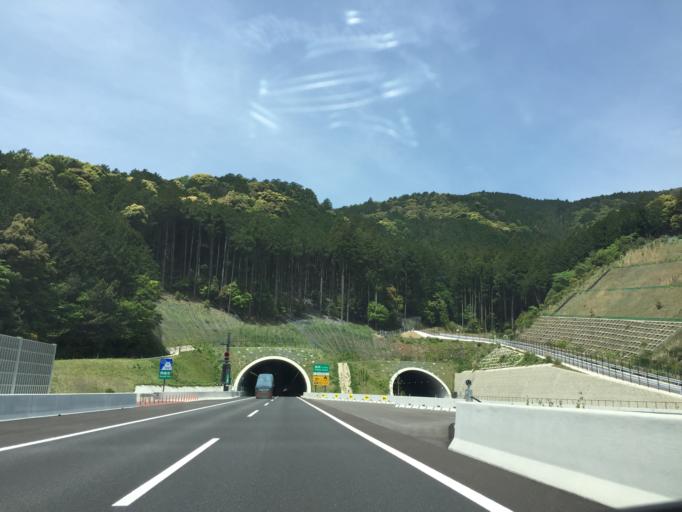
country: JP
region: Aichi
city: Kozakai-cho
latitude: 34.8963
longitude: 137.3307
